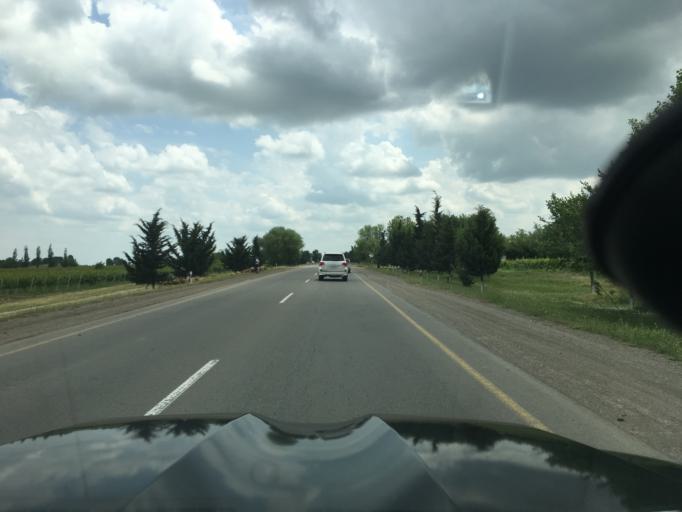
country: AZ
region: Tovuz
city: Tovuz
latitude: 40.9695
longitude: 45.6928
